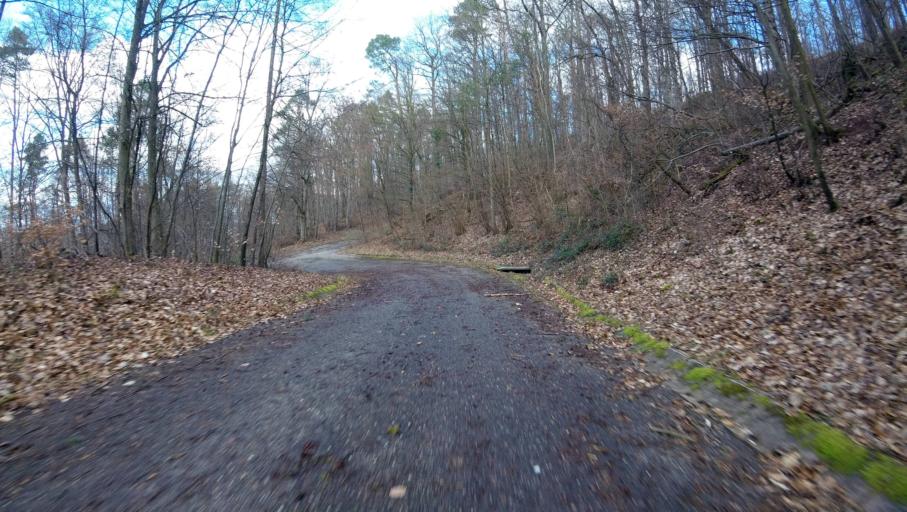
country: DE
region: Baden-Wuerttemberg
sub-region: Regierungsbezirk Stuttgart
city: Grossbottwar
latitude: 48.9961
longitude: 9.3150
